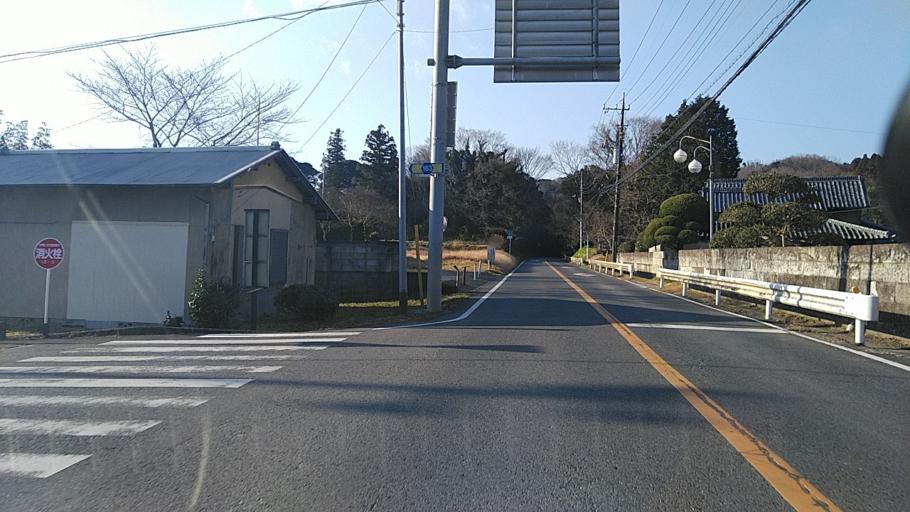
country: JP
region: Chiba
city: Kimitsu
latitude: 35.2944
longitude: 139.9789
